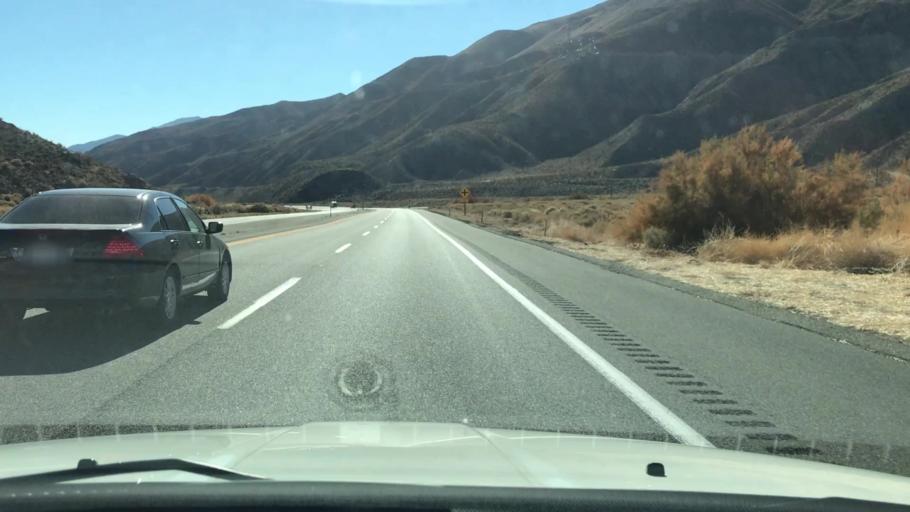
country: US
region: California
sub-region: Kern County
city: Inyokern
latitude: 35.9314
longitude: -117.9067
